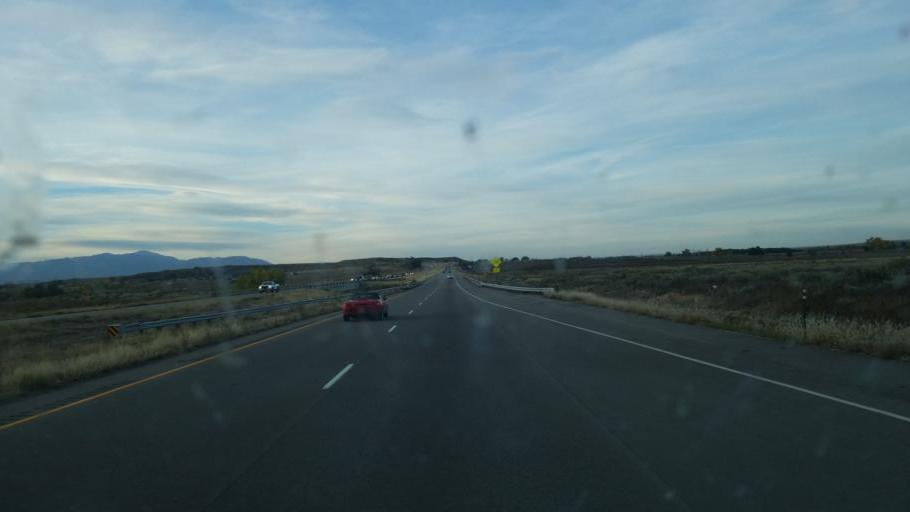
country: US
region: Colorado
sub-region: Pueblo County
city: Pueblo West
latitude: 38.4872
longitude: -104.6205
